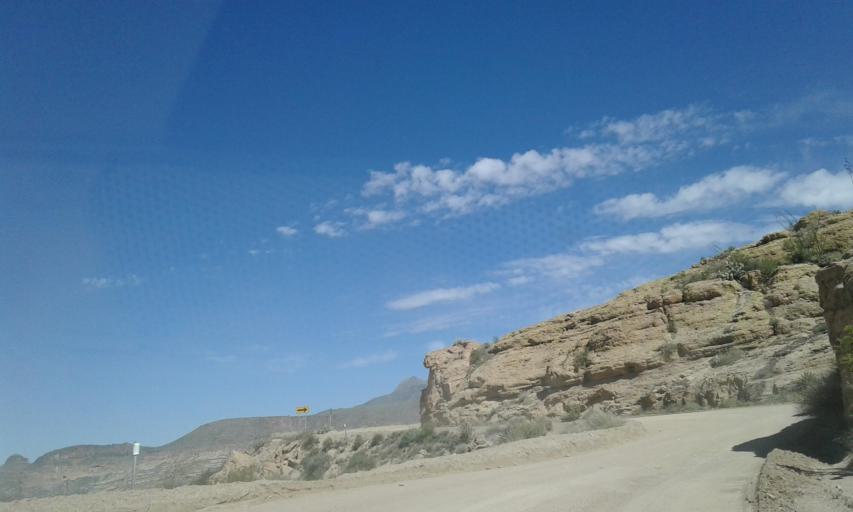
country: US
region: Arizona
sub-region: Pinal County
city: Gold Camp
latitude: 33.5281
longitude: -111.3168
